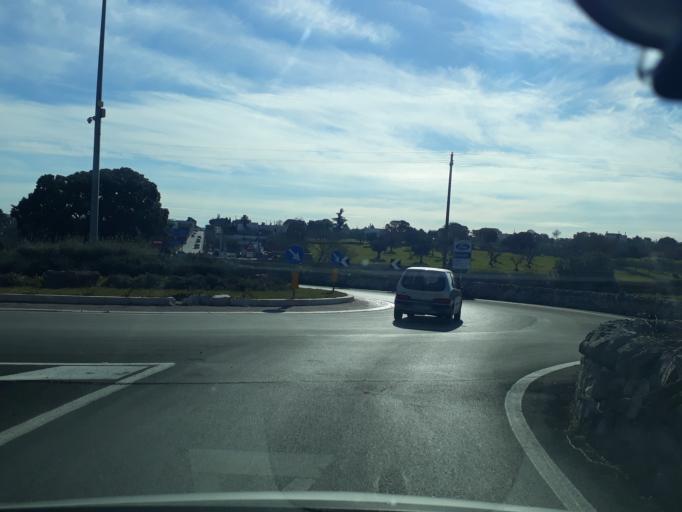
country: IT
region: Apulia
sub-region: Provincia di Bari
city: Locorotondo
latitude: 40.7494
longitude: 17.3294
